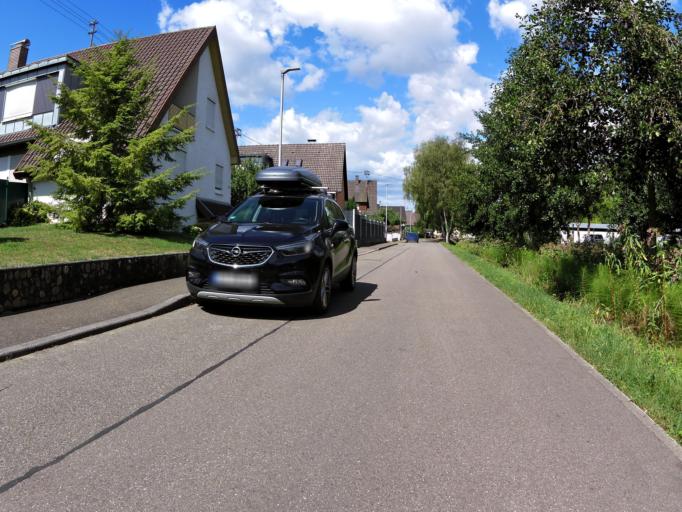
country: DE
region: Baden-Wuerttemberg
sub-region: Freiburg Region
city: Lahr
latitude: 48.3064
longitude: 7.8683
